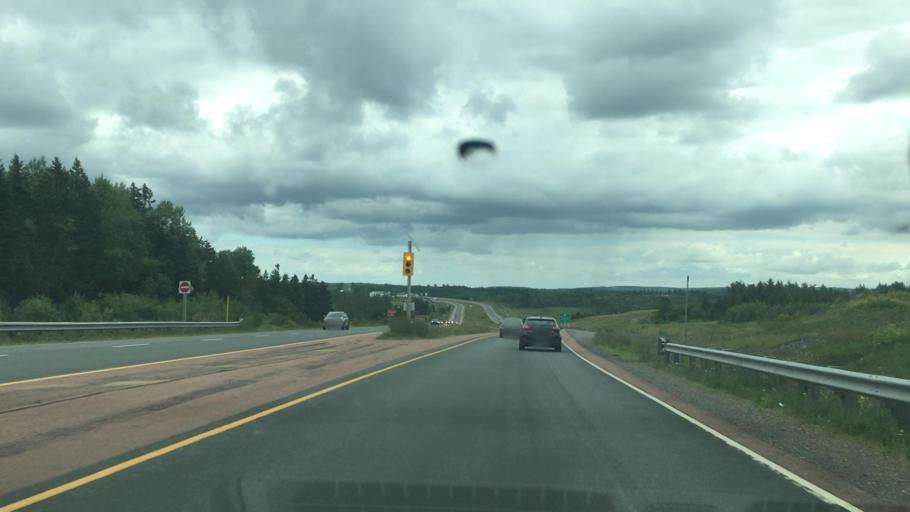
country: CA
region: Nova Scotia
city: Antigonish
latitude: 45.5968
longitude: -62.0482
